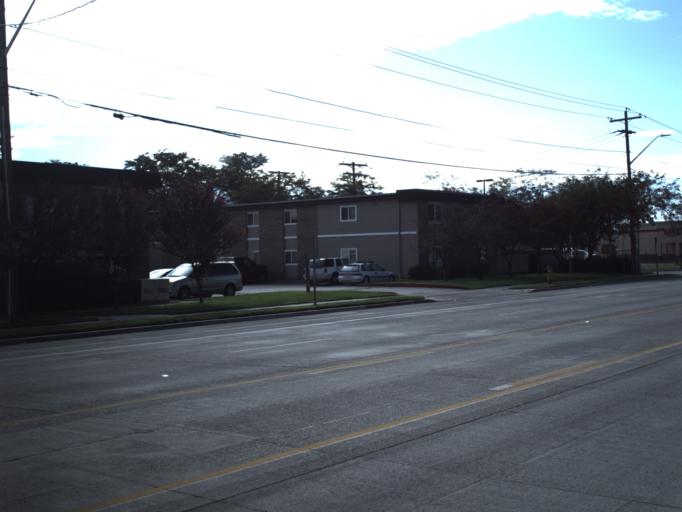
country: US
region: Utah
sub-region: Salt Lake County
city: Salt Lake City
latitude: 40.7735
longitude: -111.9394
